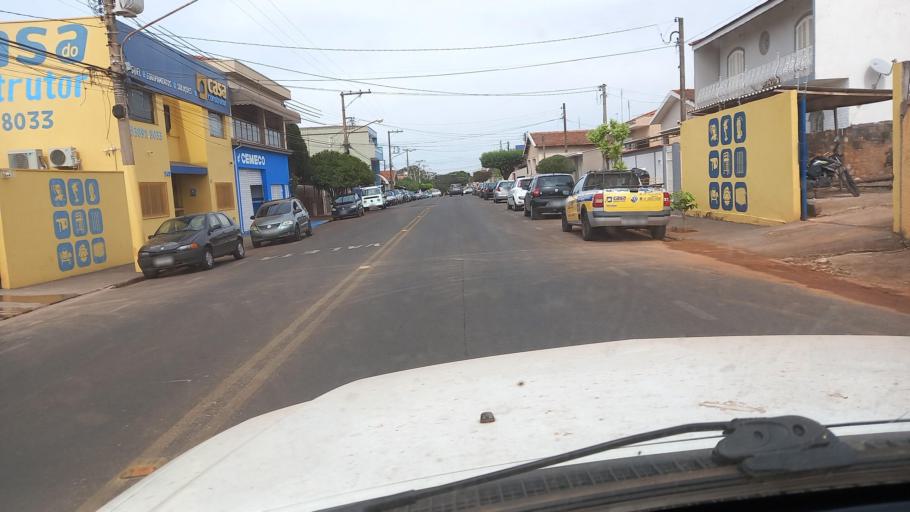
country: BR
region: Sao Paulo
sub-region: Moji-Guacu
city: Mogi-Gaucu
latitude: -22.3604
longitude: -46.9422
